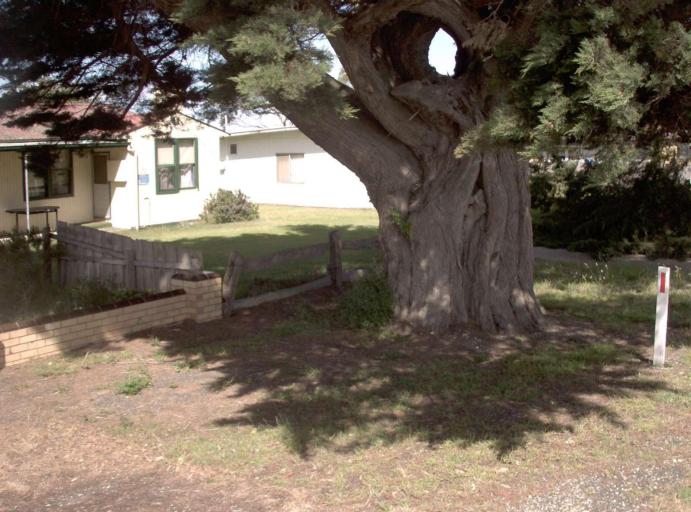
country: AU
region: Victoria
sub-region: Wellington
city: Sale
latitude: -38.3678
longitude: 147.1895
